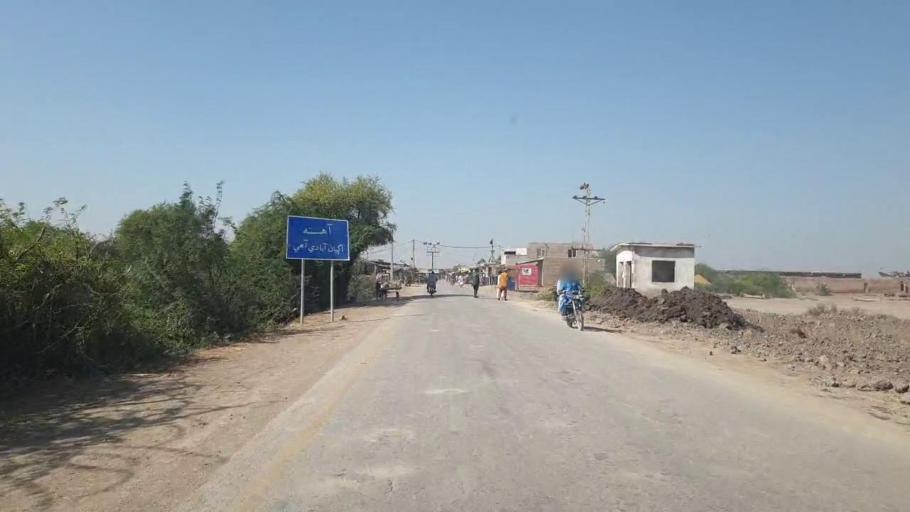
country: PK
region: Sindh
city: Rajo Khanani
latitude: 25.0597
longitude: 68.8011
